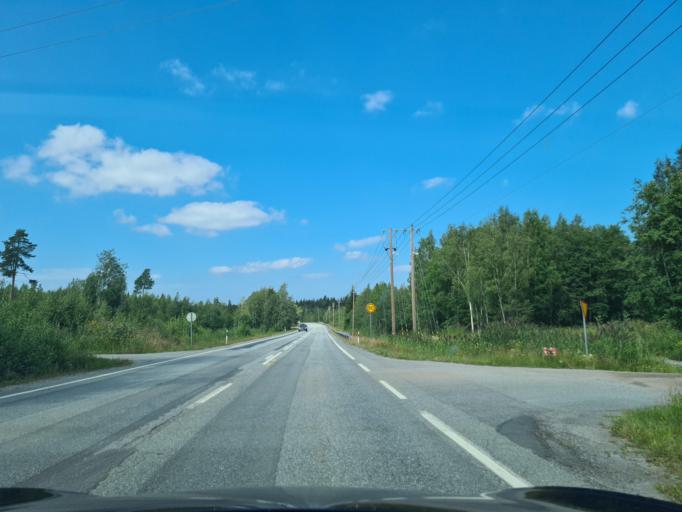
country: FI
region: Ostrobothnia
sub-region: Vaasa
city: Vaasa
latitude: 63.1864
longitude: 21.5663
